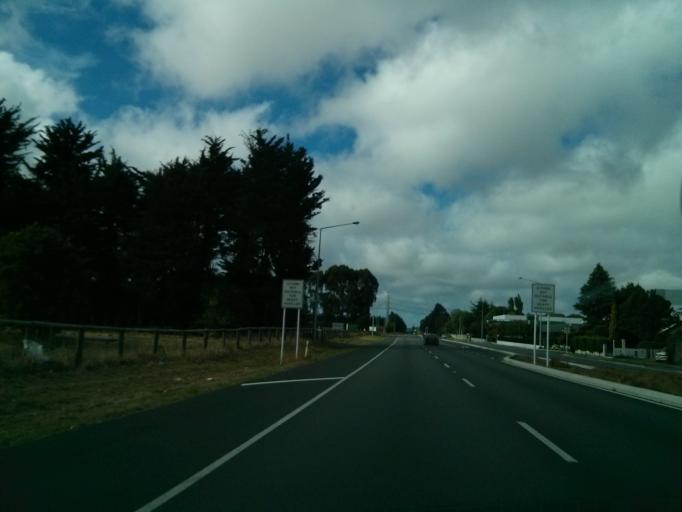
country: NZ
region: Canterbury
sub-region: Selwyn District
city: Prebbleton
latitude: -43.5154
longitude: 172.5369
